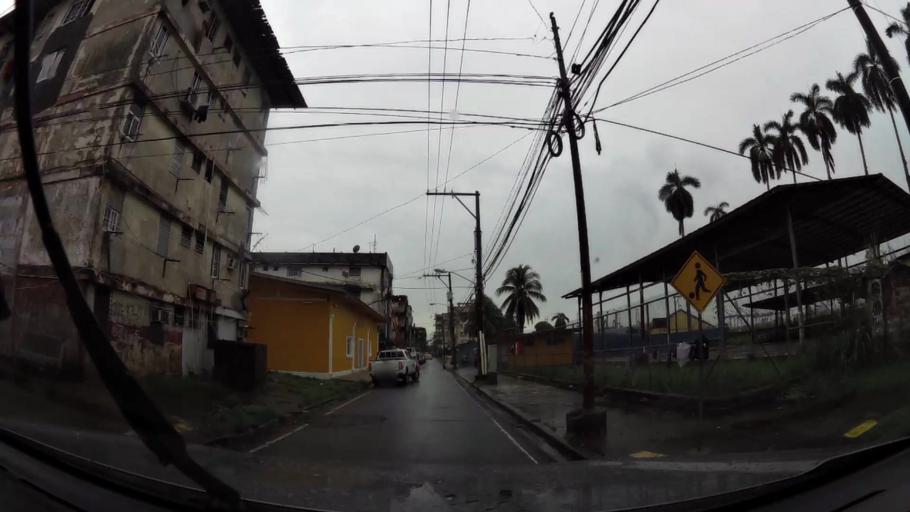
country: PA
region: Colon
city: Colon
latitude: 9.3627
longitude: -79.9058
